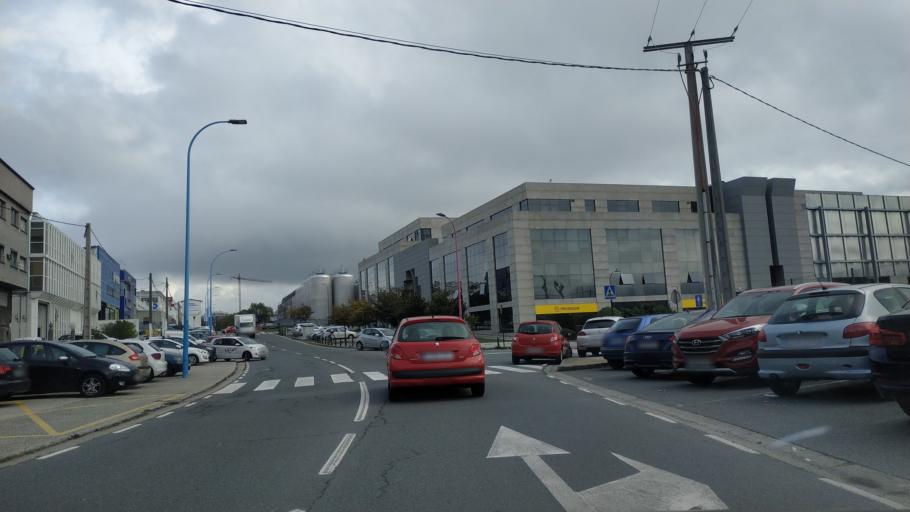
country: ES
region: Galicia
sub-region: Provincia da Coruna
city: A Coruna
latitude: 43.3548
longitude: -8.4234
